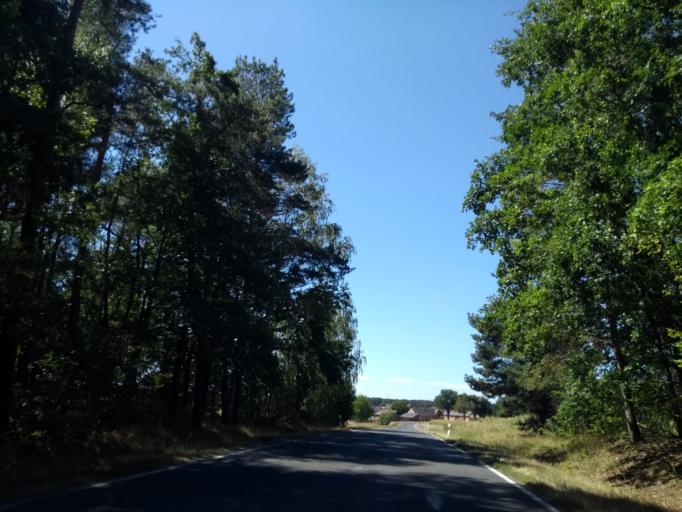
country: DE
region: Brandenburg
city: Sallgast
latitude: 51.6005
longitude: 13.7836
